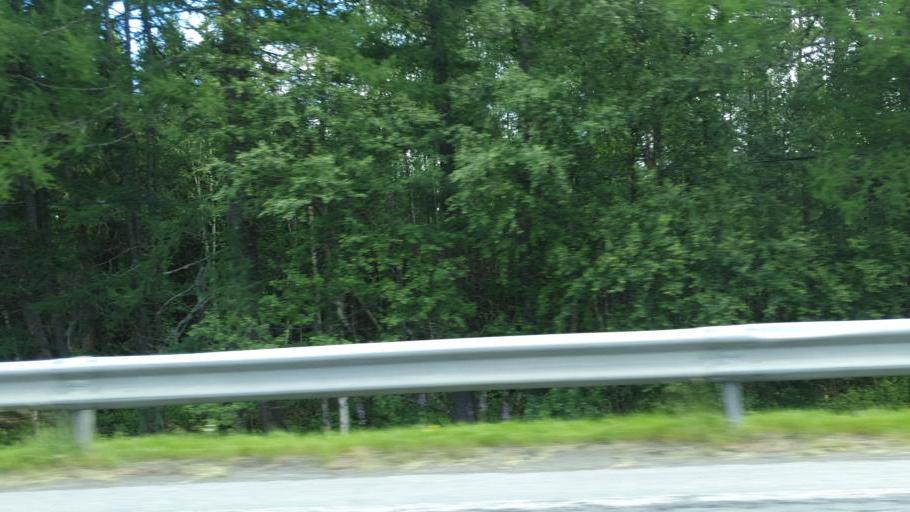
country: NO
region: Sor-Trondelag
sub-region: Rennebu
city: Berkak
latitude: 62.6848
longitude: 9.9295
